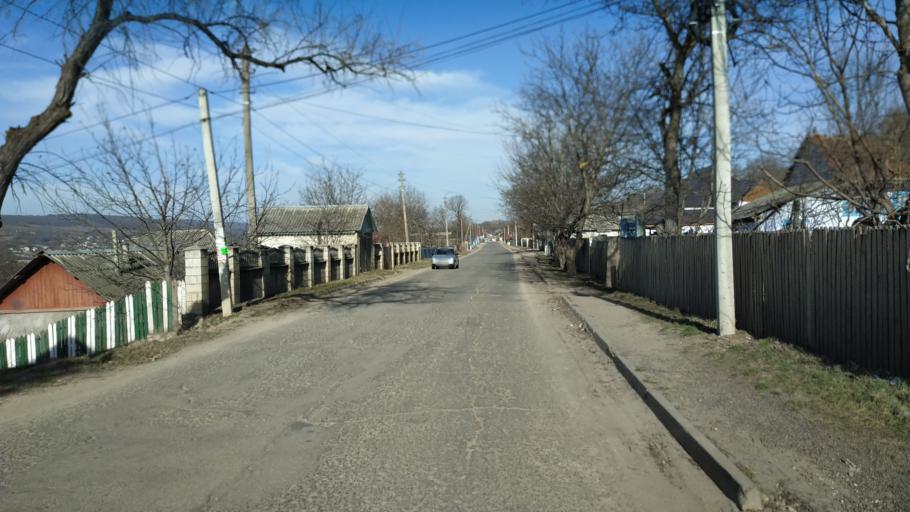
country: MD
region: Chisinau
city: Vatra
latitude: 47.0227
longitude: 28.6420
